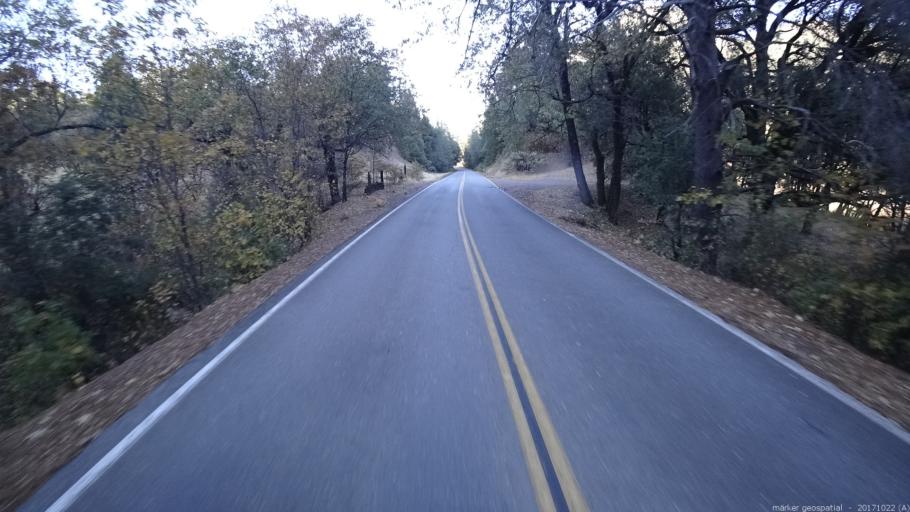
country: US
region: California
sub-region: Siskiyou County
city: Dunsmuir
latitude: 40.9332
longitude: -122.2505
